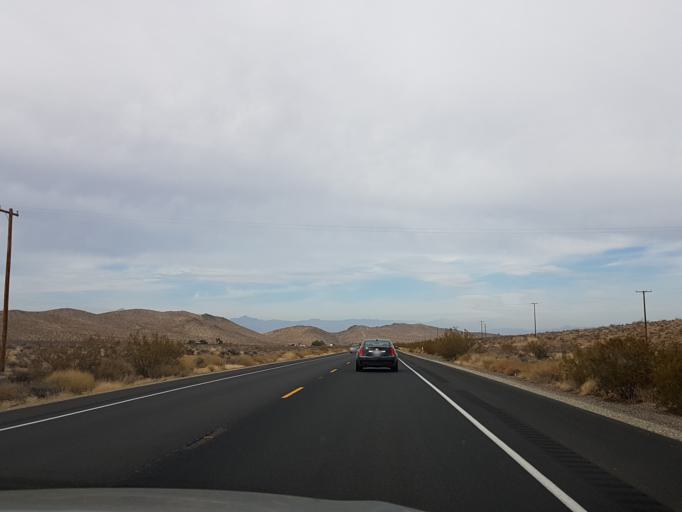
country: US
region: California
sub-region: Kern County
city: Ridgecrest
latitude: 35.5267
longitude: -117.6774
